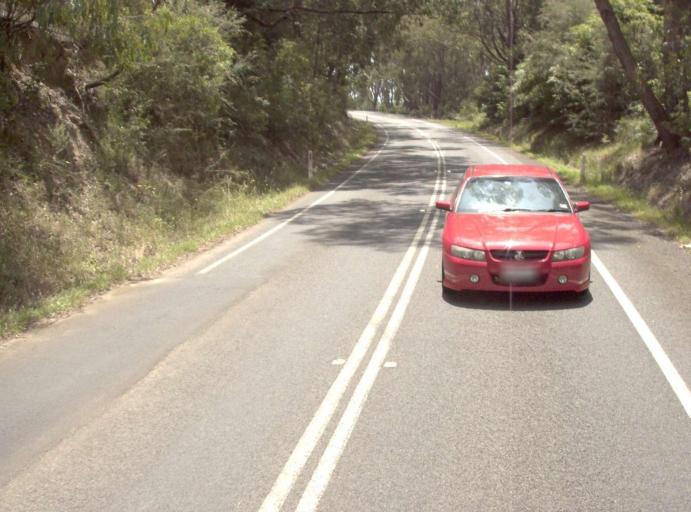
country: AU
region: Victoria
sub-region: Latrobe
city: Traralgon
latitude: -38.3707
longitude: 146.7568
